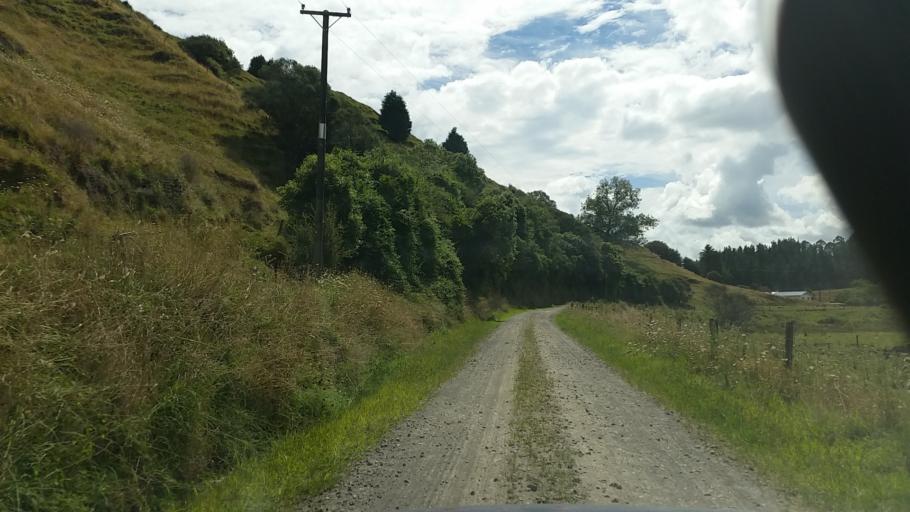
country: NZ
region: Taranaki
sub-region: South Taranaki District
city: Eltham
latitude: -39.2605
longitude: 174.5665
